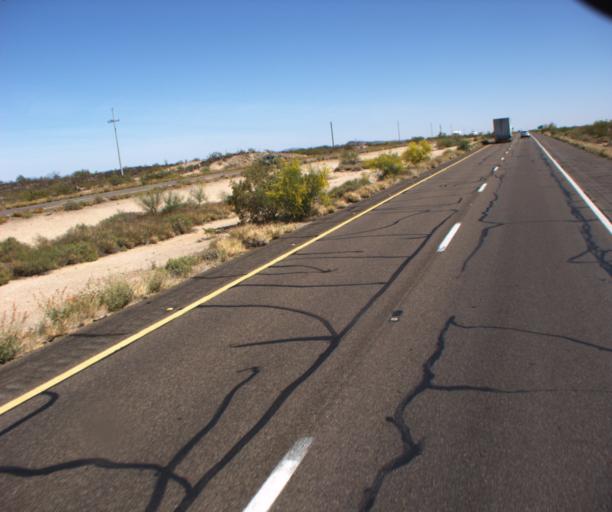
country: US
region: Arizona
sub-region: Maricopa County
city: Gila Bend
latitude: 32.8560
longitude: -113.2416
